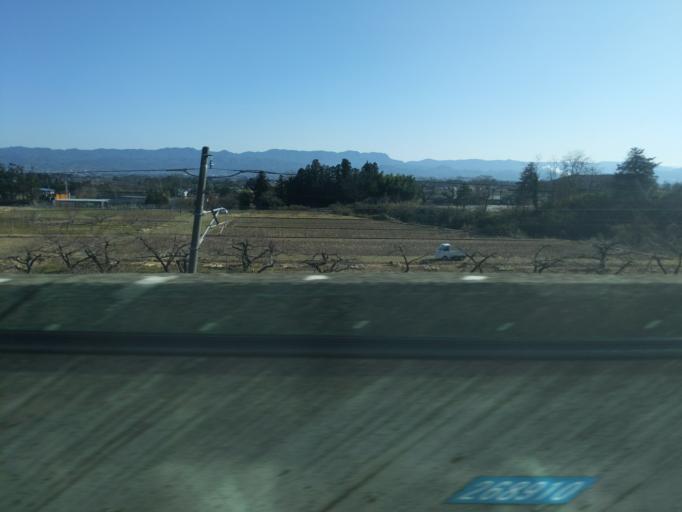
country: JP
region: Fukushima
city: Hobaramachi
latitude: 37.8653
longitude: 140.5250
